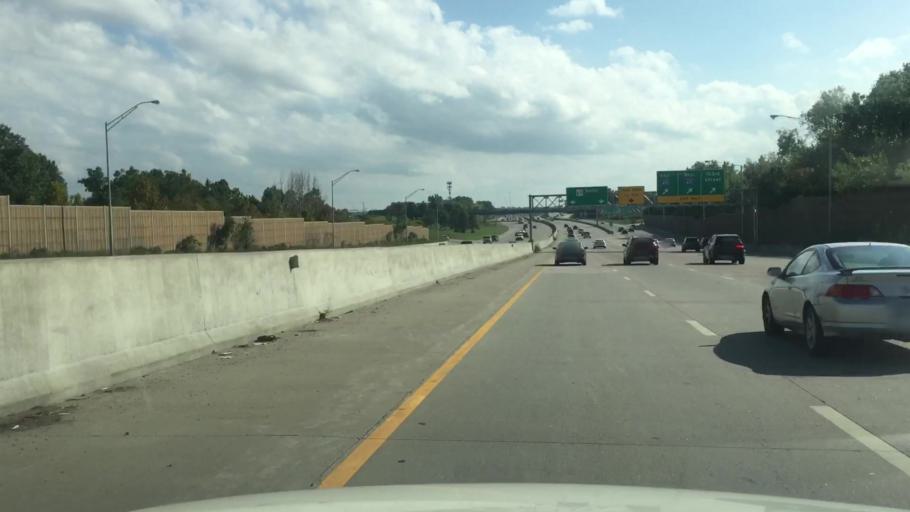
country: US
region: Kansas
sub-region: Johnson County
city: Lenexa
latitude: 38.9484
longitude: -94.7056
